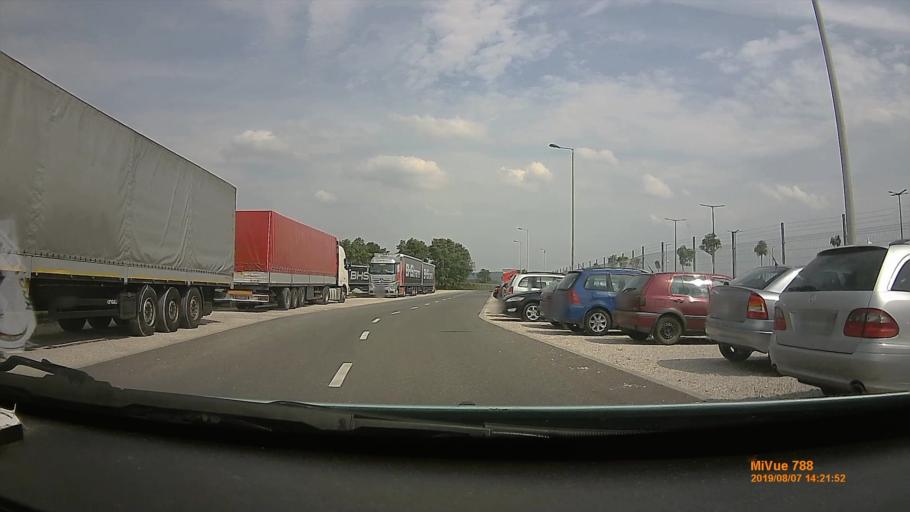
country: HU
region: Borsod-Abauj-Zemplen
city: Szikszo
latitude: 48.1760
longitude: 20.9227
